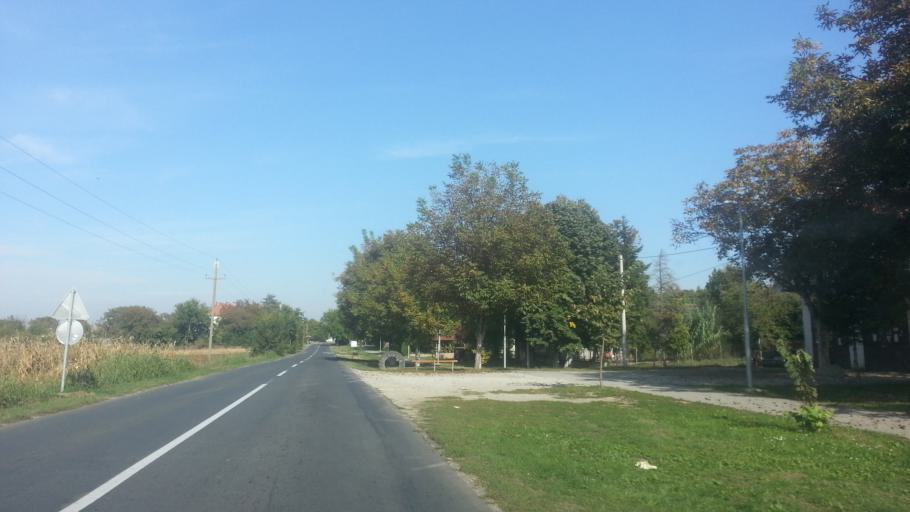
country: RS
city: Belegis
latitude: 45.0068
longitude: 20.3130
